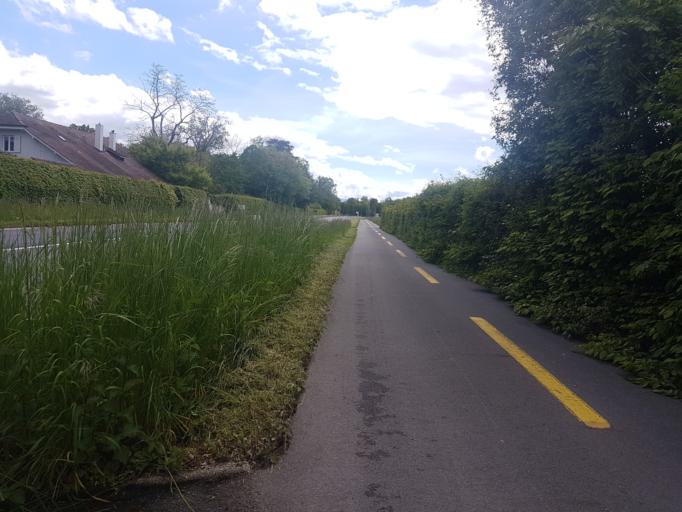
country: CH
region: Vaud
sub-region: Nyon District
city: Founex
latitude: 46.3451
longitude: 6.2060
